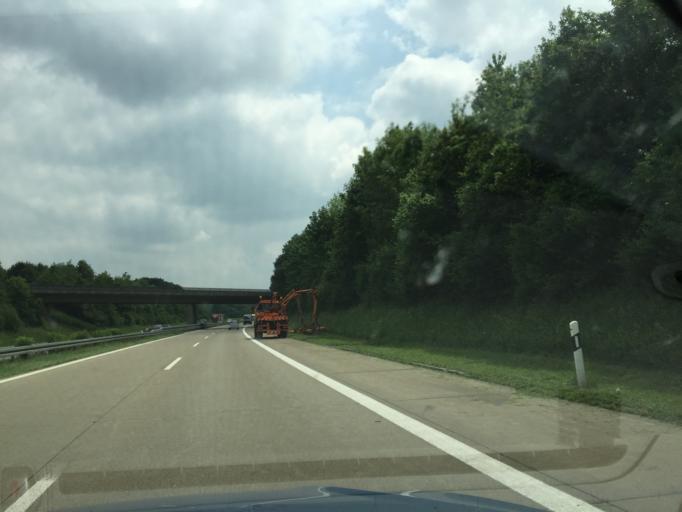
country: DE
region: Baden-Wuerttemberg
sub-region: Regierungsbezirk Stuttgart
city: Lauchheim
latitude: 48.8315
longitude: 10.2104
